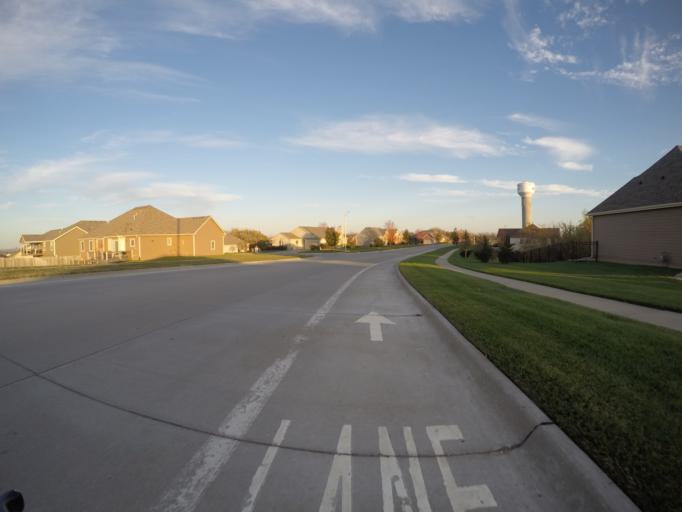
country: US
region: Kansas
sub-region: Riley County
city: Manhattan
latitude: 39.1689
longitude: -96.6268
